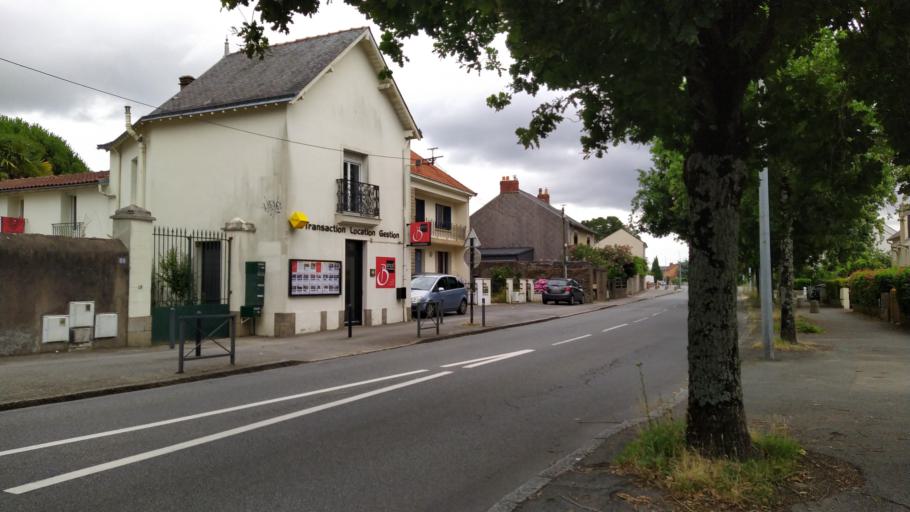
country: FR
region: Pays de la Loire
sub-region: Departement de la Loire-Atlantique
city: Saint-Sebastien-sur-Loire
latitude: 47.2320
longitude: -1.5150
